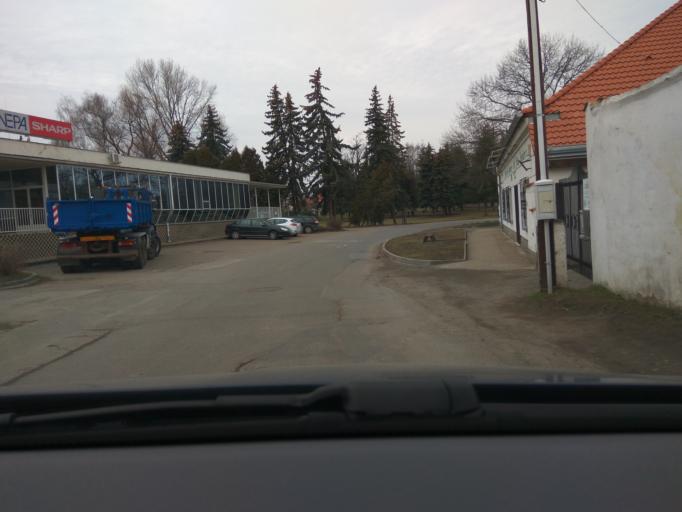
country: CZ
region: Central Bohemia
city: Hovorcovice
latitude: 50.1797
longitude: 14.5190
